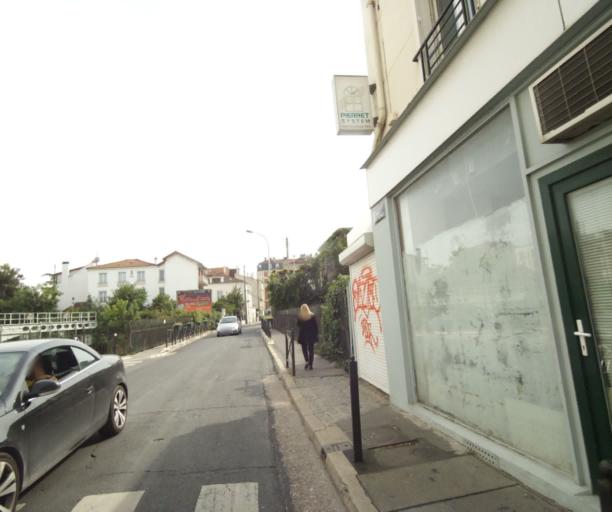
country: FR
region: Ile-de-France
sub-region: Departement des Hauts-de-Seine
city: Bois-Colombes
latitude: 48.9181
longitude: 2.2664
